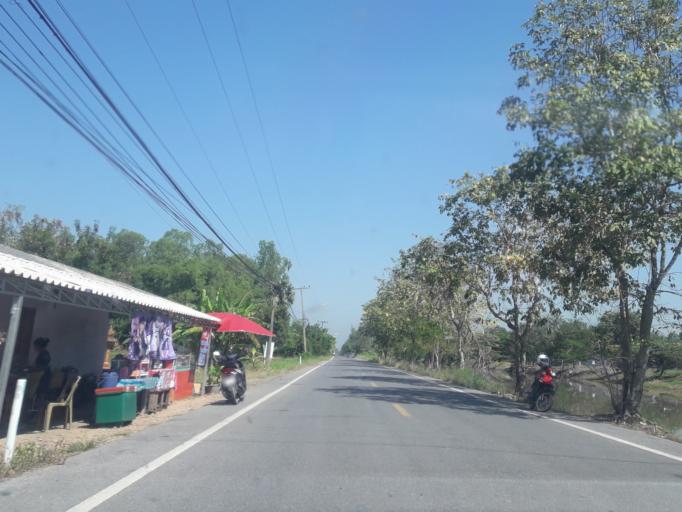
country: TH
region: Pathum Thani
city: Nong Suea
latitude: 14.1509
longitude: 100.8459
